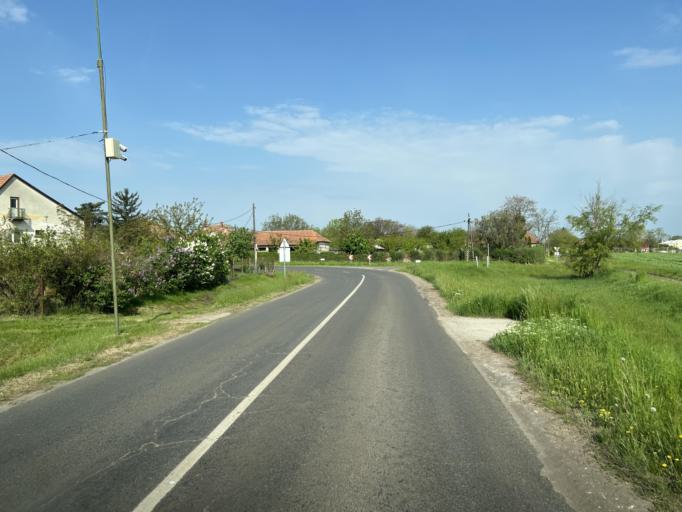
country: HU
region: Pest
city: Jaszkarajeno
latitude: 47.0497
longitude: 20.0782
